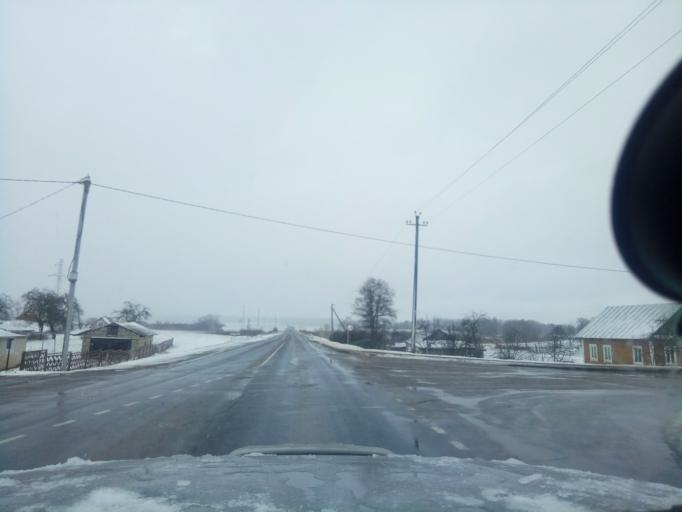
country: BY
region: Minsk
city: Nyasvizh
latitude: 53.2085
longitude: 26.6625
